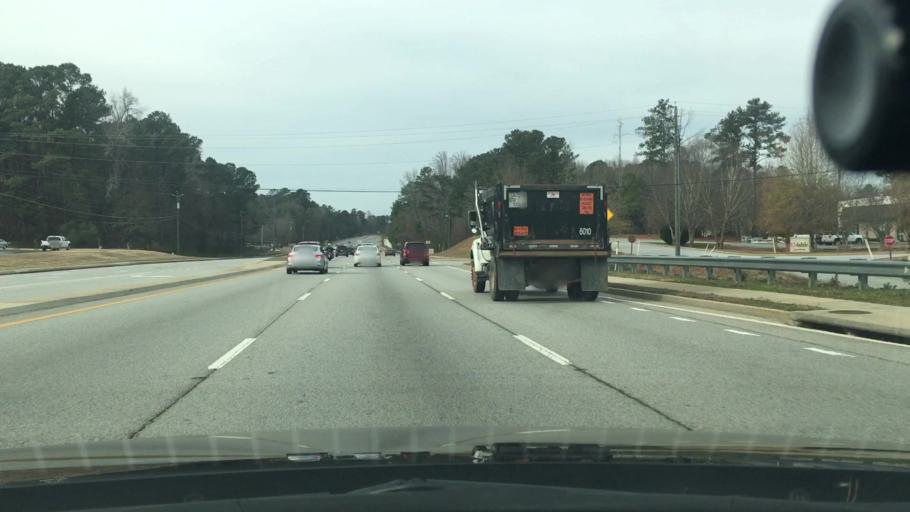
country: US
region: Georgia
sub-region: Fayette County
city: Peachtree City
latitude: 33.3747
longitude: -84.5715
